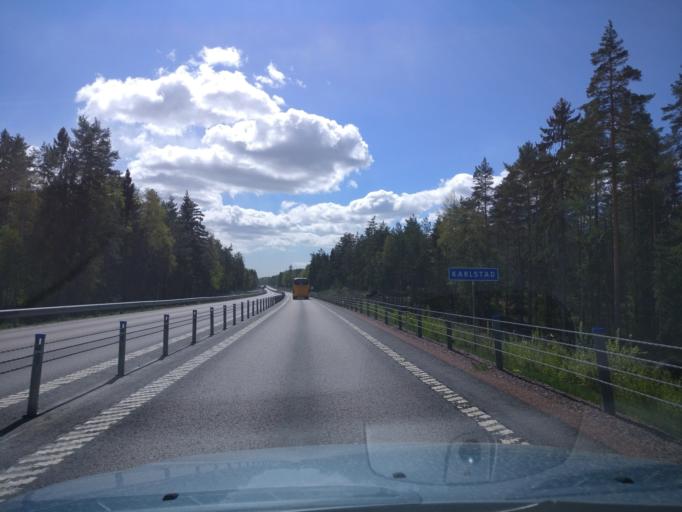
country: SE
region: Vaermland
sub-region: Karlstads Kommun
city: Karlstad
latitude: 59.4218
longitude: 13.5334
